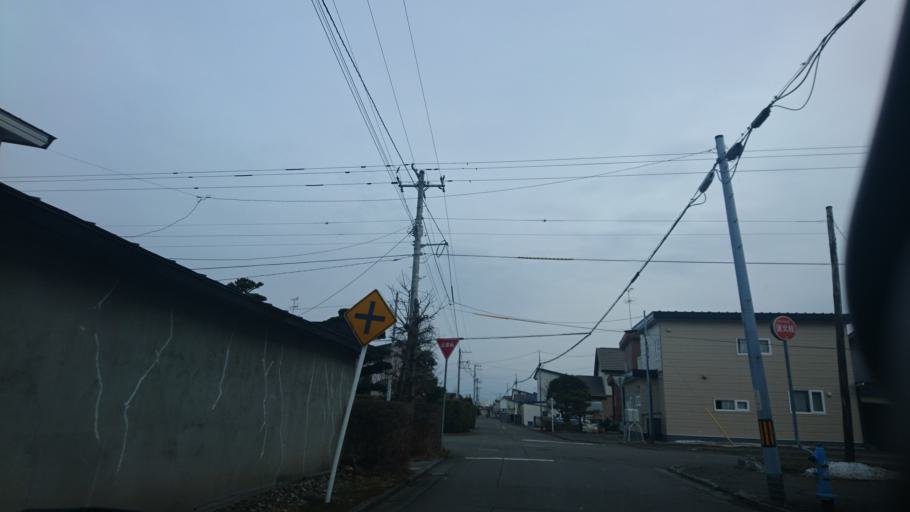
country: JP
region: Hokkaido
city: Otofuke
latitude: 42.9953
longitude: 143.1994
